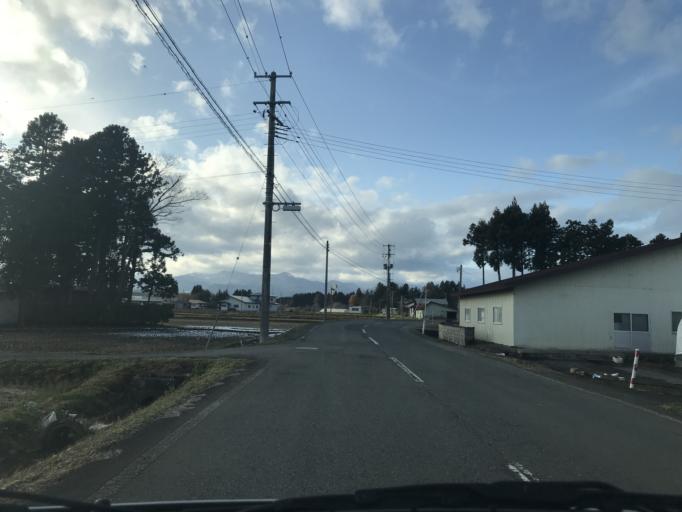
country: JP
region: Iwate
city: Mizusawa
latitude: 39.1877
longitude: 141.0972
